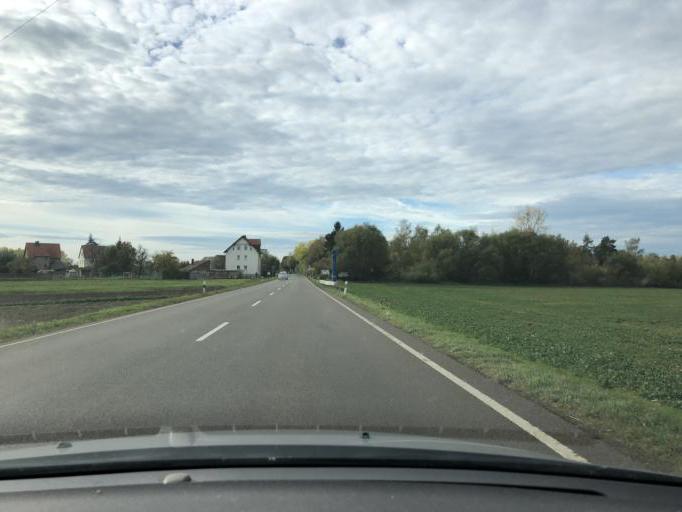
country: DE
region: Saxony
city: Elstertrebnitz
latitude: 51.1333
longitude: 12.2215
